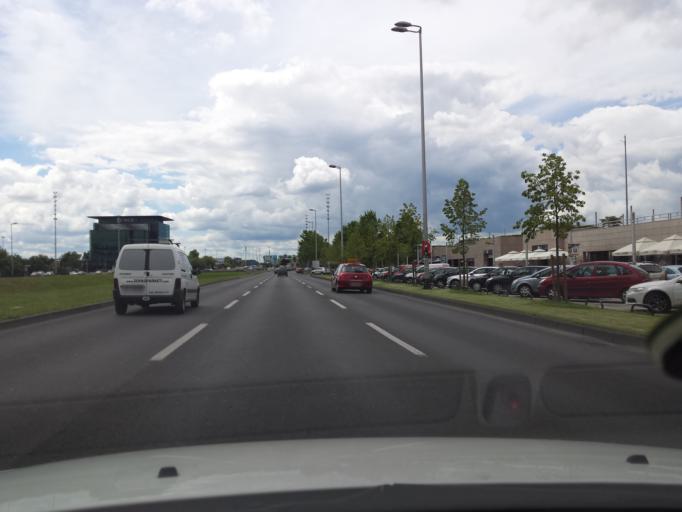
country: HR
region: Grad Zagreb
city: Novi Zagreb
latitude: 45.7972
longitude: 15.9788
